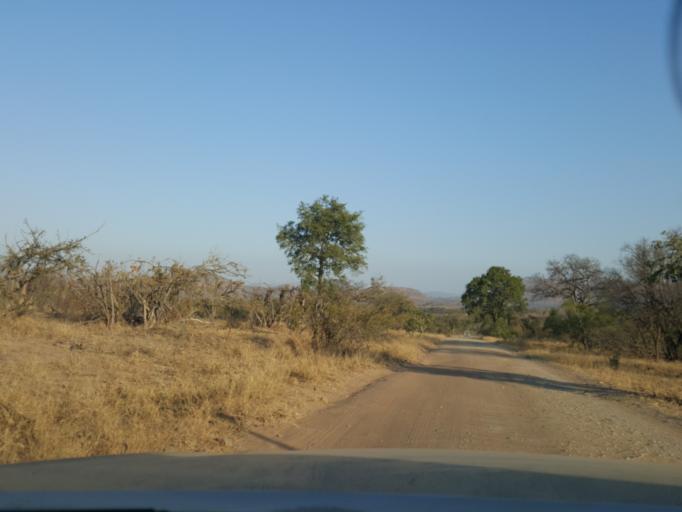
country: SZ
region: Hhohho
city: Ntfonjeni
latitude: -25.4118
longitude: 31.4404
